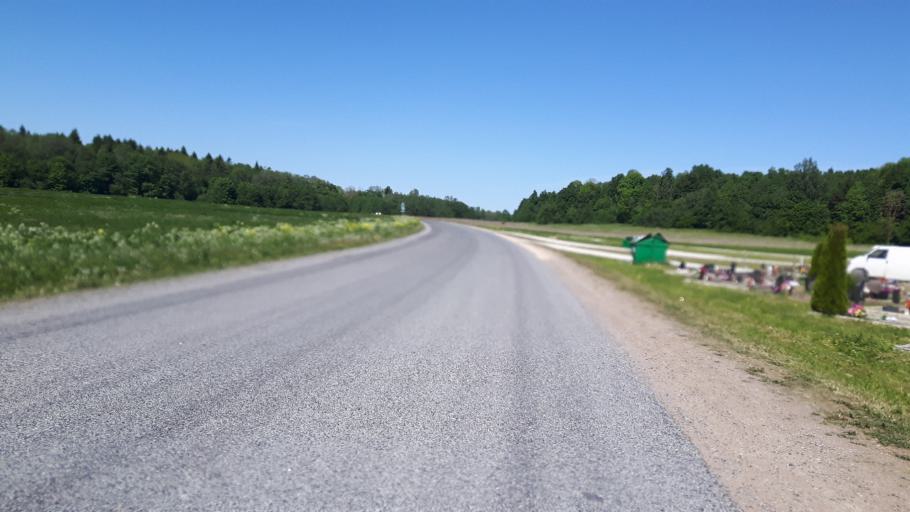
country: EE
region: Ida-Virumaa
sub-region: Sillamaee linn
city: Sillamae
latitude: 59.3736
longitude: 27.8425
